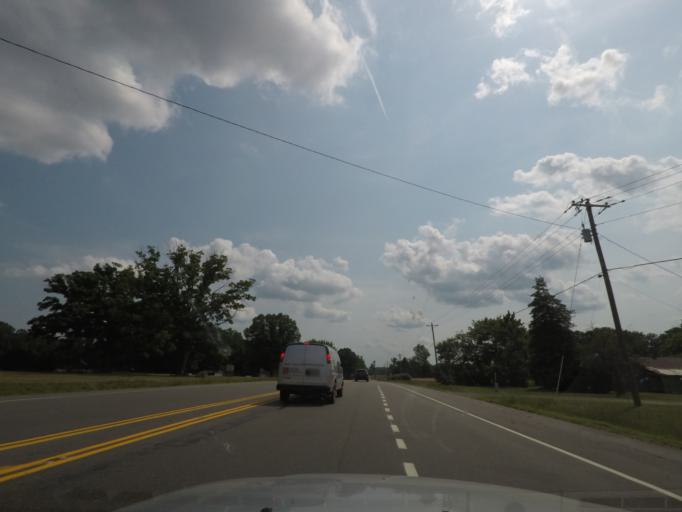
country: US
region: Virginia
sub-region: Fluvanna County
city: Palmyra
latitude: 37.9687
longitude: -78.2214
